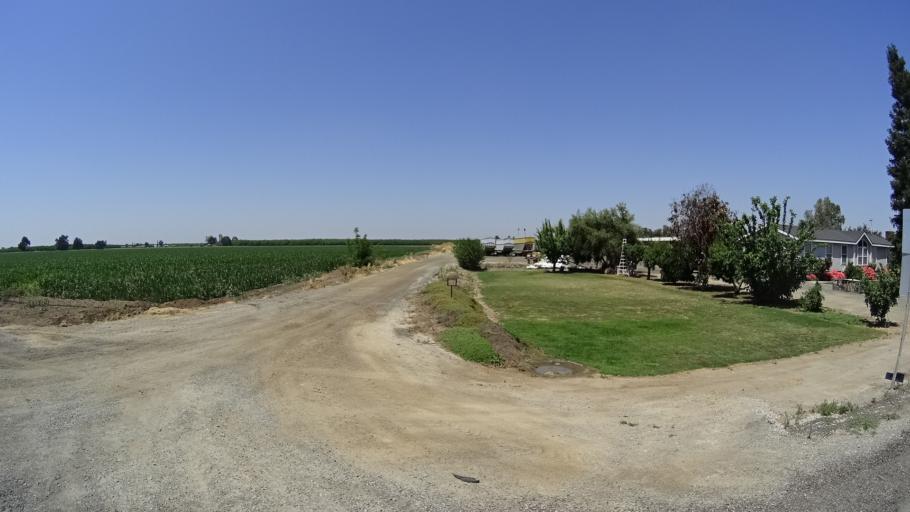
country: US
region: California
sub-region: Fresno County
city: Laton
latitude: 36.4214
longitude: -119.6864
